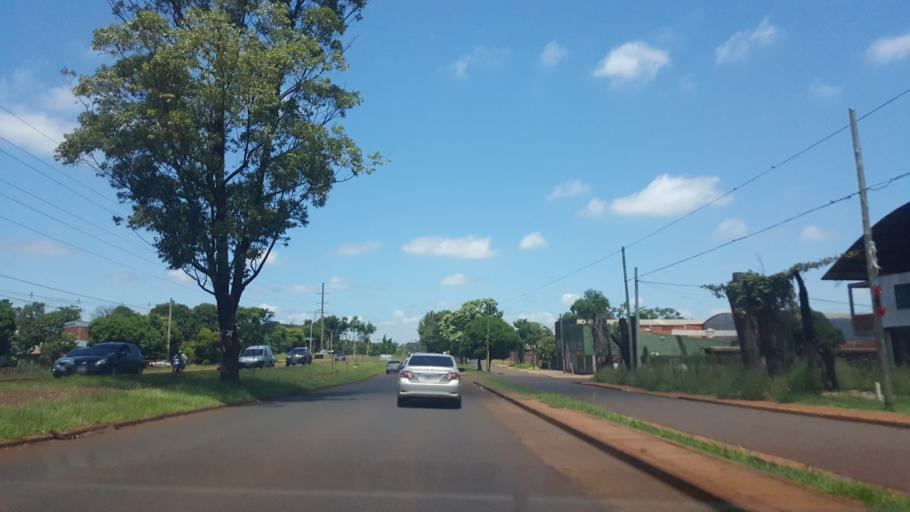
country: AR
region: Misiones
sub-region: Departamento de Capital
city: Posadas
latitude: -27.4132
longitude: -55.9276
